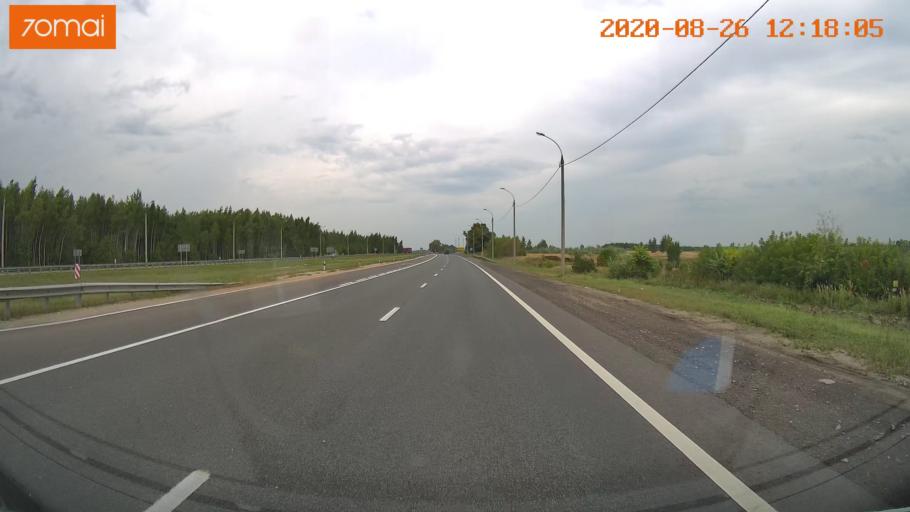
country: RU
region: Rjazan
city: Murmino
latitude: 54.4696
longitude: 40.0245
